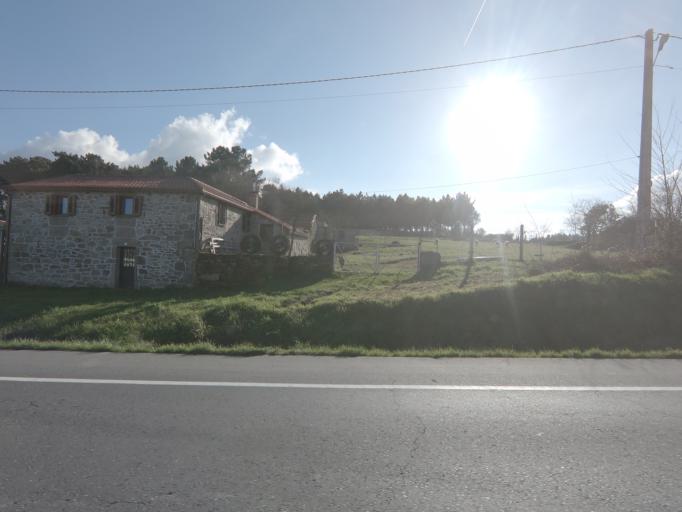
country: ES
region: Galicia
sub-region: Provincia de Pontevedra
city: Silleda
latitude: 42.7214
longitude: -8.2864
